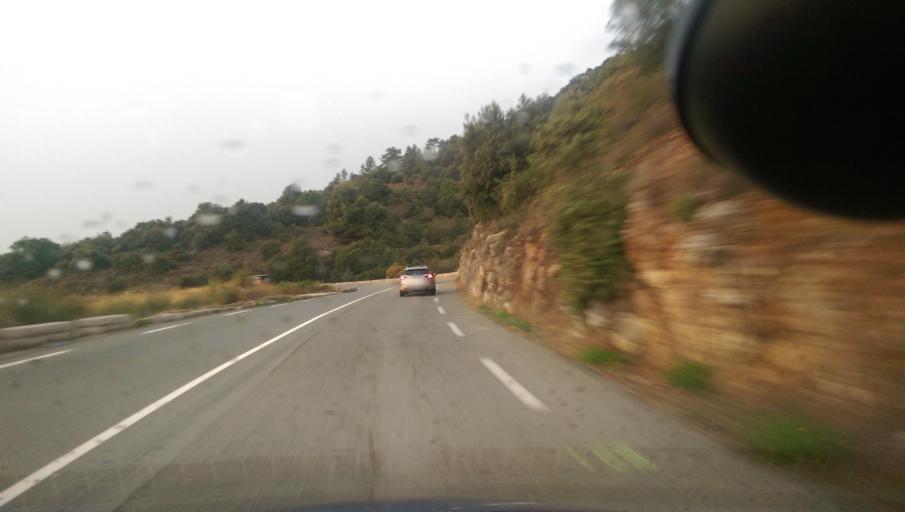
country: FR
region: Provence-Alpes-Cote d'Azur
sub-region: Departement des Alpes-Maritimes
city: Grasse
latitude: 43.6790
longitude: 6.8965
